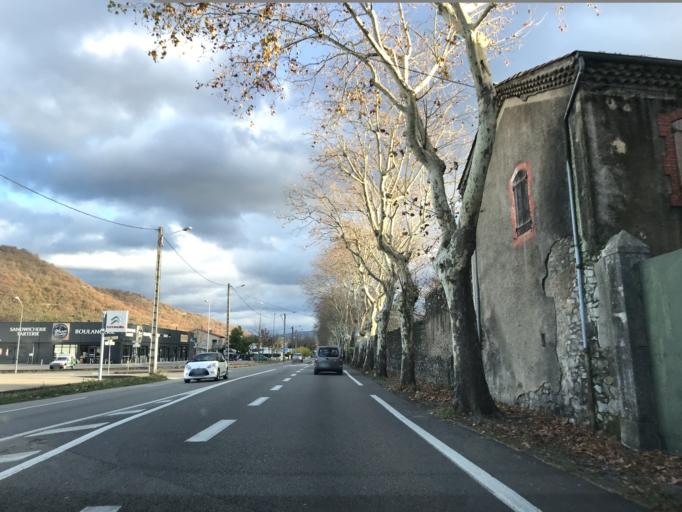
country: FR
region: Rhone-Alpes
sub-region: Departement de l'Ardeche
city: Privas
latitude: 44.7196
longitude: 4.6031
